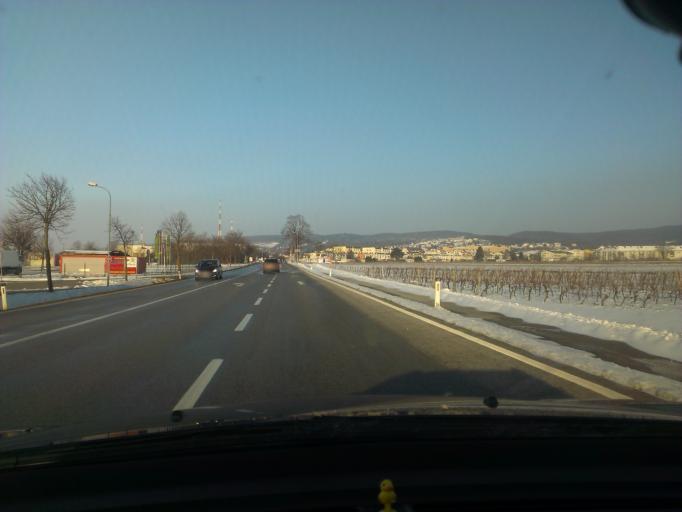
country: AT
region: Burgenland
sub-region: Eisenstadt Stadt
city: Eisenstadt
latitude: 47.8453
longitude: 16.5483
